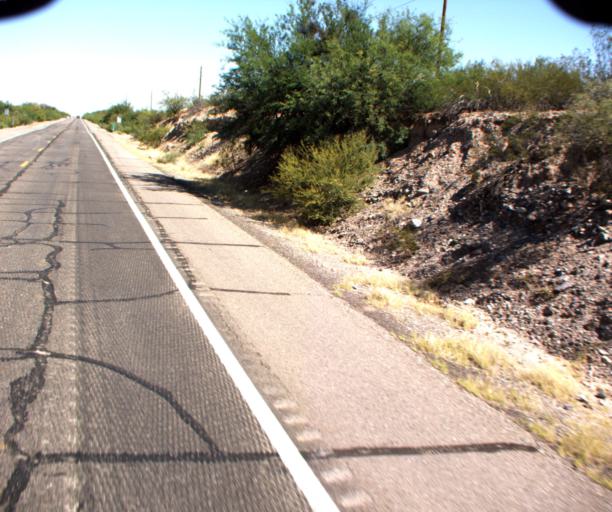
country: US
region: Arizona
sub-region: Pinal County
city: Mammoth
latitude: 32.7833
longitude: -110.6676
